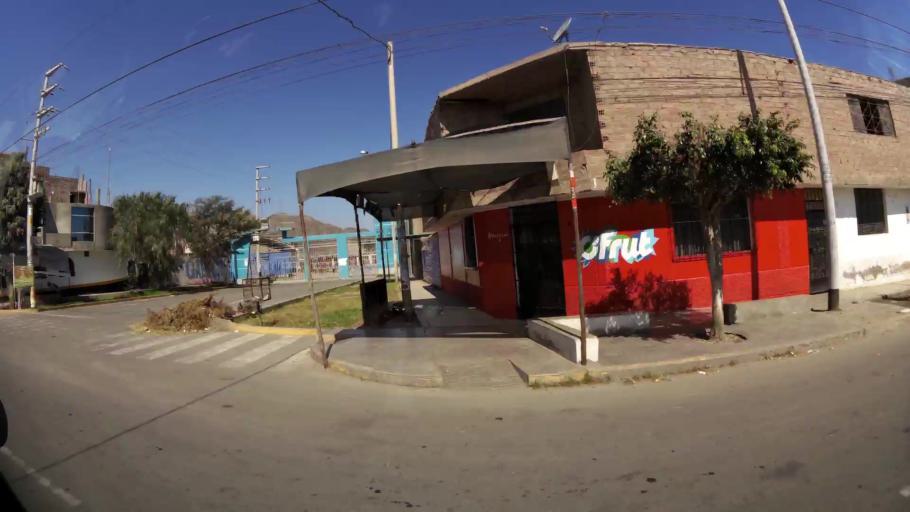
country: PE
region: Ica
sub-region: Provincia de Ica
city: La Tinguina
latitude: -14.0449
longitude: -75.6964
